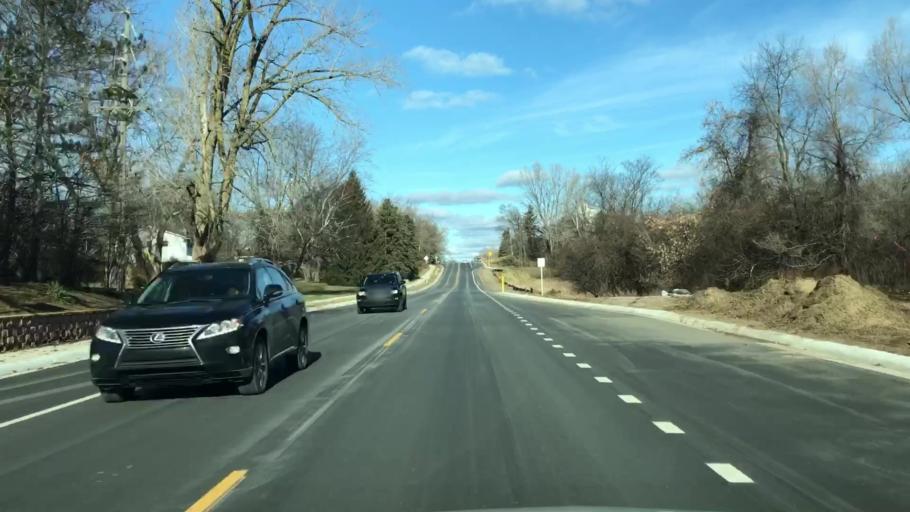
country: US
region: Michigan
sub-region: Oakland County
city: Bloomfield Hills
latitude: 42.6158
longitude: -83.2089
